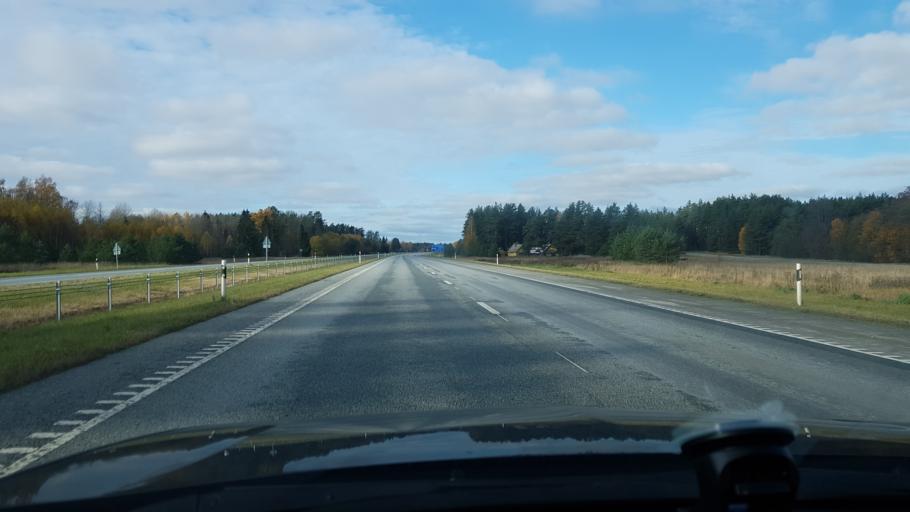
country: EE
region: Laeaene-Virumaa
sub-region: Kadrina vald
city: Kadrina
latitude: 59.4464
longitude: 26.0851
